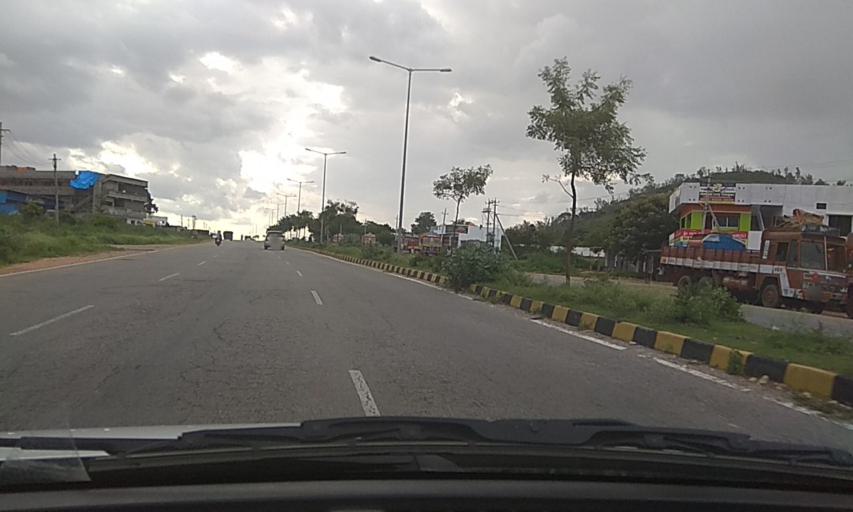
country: IN
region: Karnataka
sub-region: Mysore
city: Mysore
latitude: 12.2598
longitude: 76.6819
